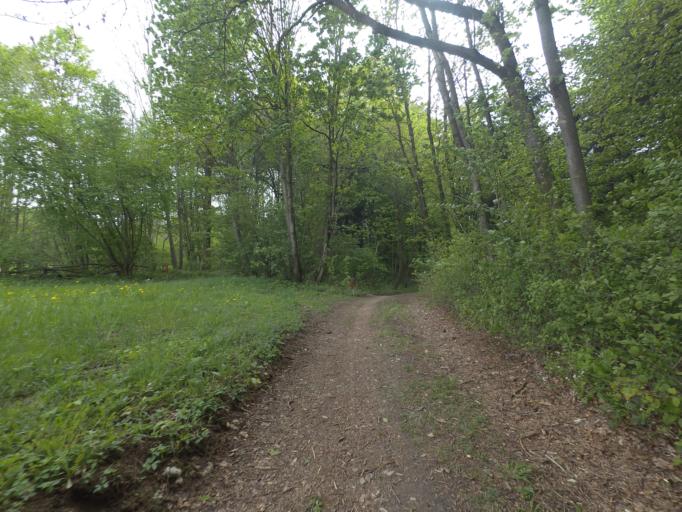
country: AT
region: Salzburg
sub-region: Politischer Bezirk Salzburg-Umgebung
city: Schleedorf
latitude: 47.9817
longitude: 13.1418
